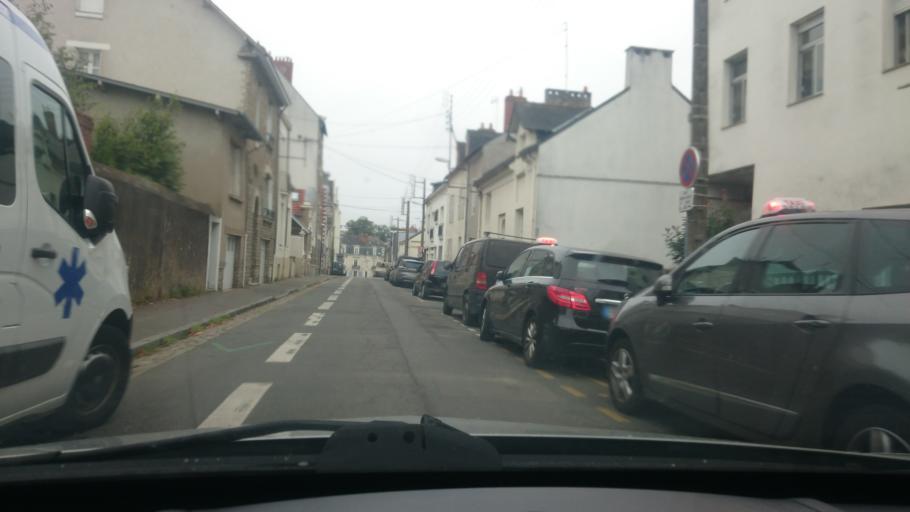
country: FR
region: Pays de la Loire
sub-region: Departement de la Loire-Atlantique
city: Nantes
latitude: 47.2178
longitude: -1.5773
